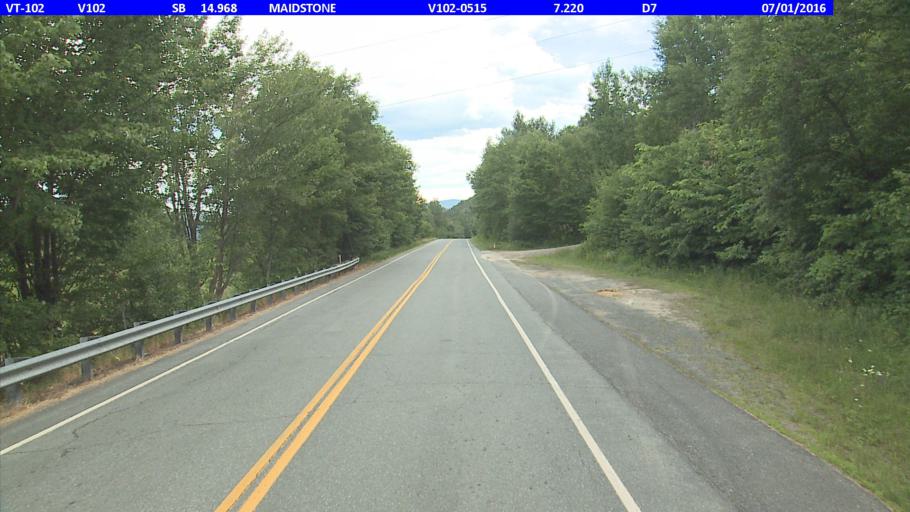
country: US
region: New Hampshire
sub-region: Coos County
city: Stratford
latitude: 44.6550
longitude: -71.5877
